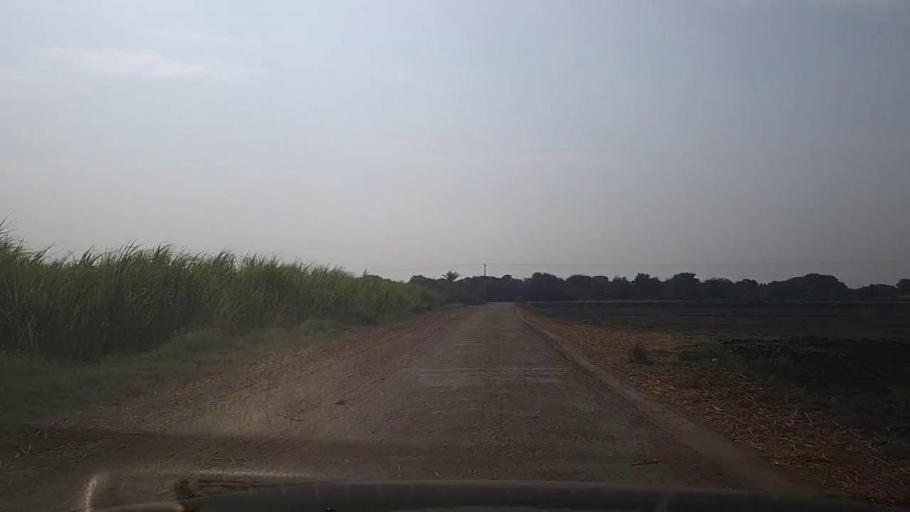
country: PK
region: Sindh
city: Bulri
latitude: 25.0090
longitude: 68.3000
